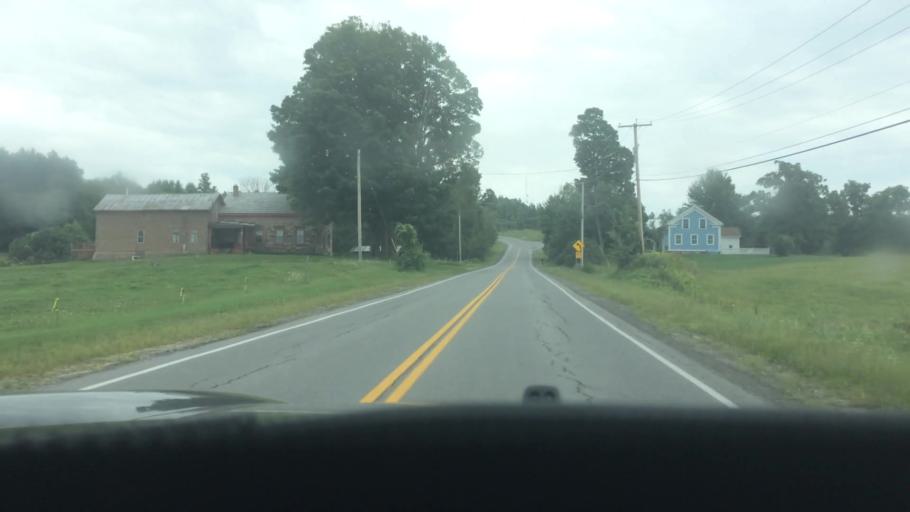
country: US
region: New York
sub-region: St. Lawrence County
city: Canton
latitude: 44.5453
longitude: -75.1020
